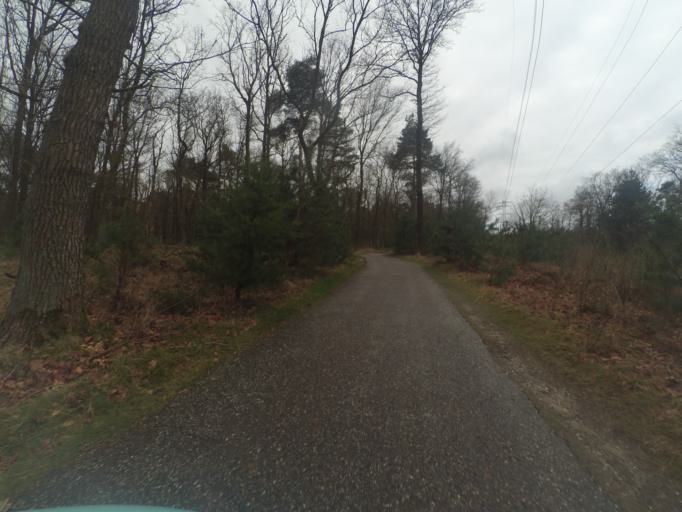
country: NL
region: Gelderland
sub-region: Gemeente Arnhem
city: Gulden Bodem
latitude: 52.0222
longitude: 5.9106
